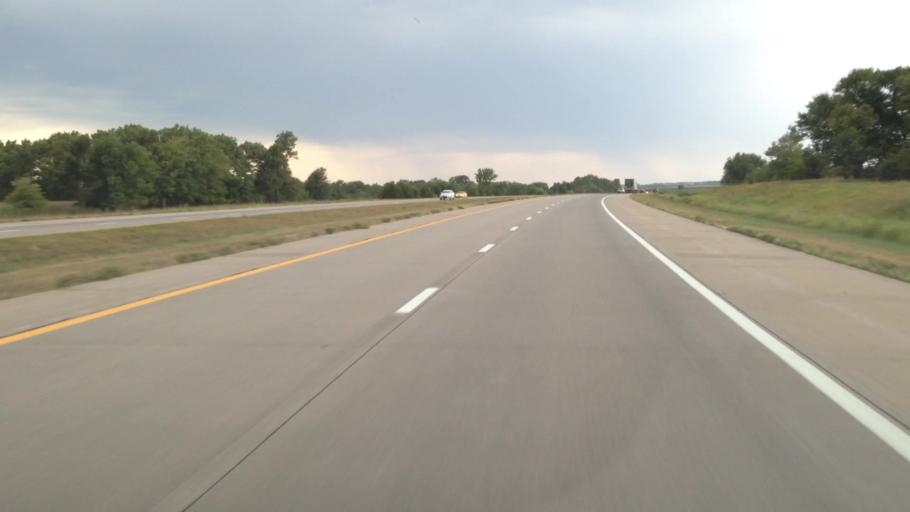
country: US
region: Kansas
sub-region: Osage County
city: Lyndon
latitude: 38.4588
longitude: -95.5532
